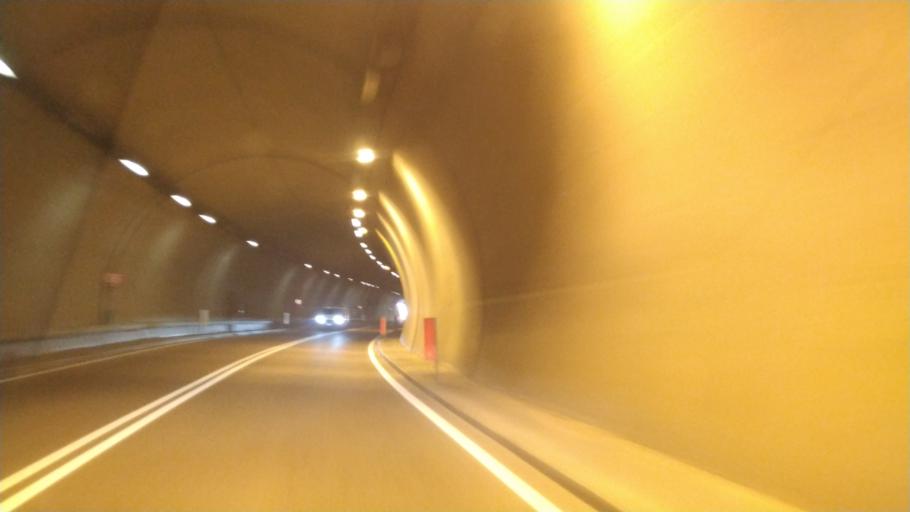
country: IT
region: Trentino-Alto Adige
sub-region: Provincia di Trento
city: Taio
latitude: 46.3198
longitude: 11.0655
